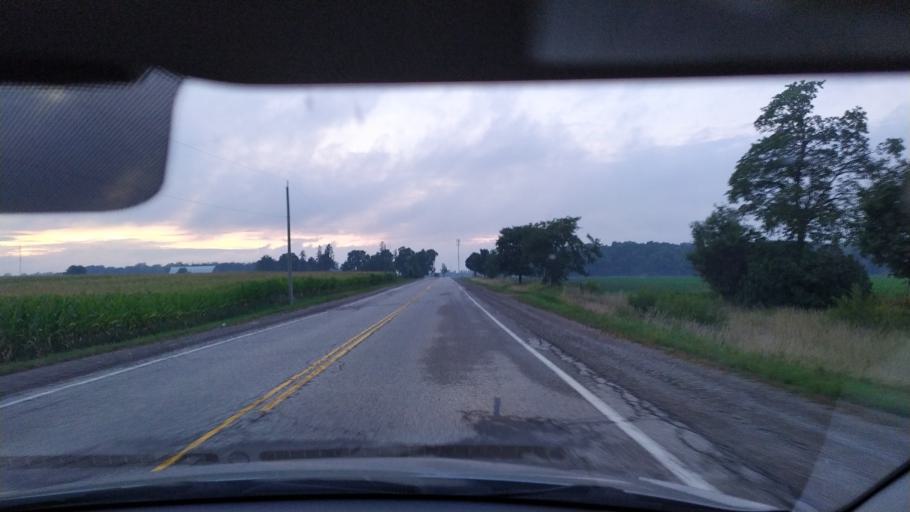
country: CA
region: Ontario
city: Kitchener
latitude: 43.3554
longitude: -80.7010
